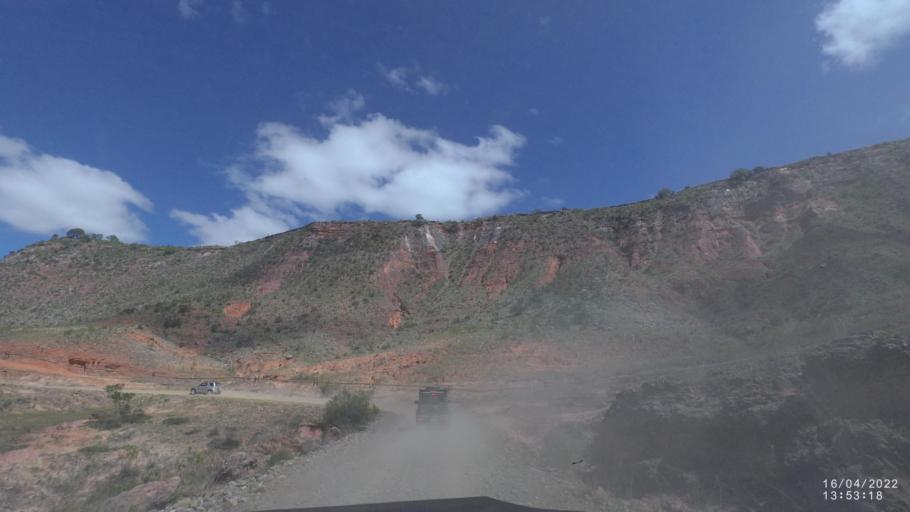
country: BO
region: Cochabamba
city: Mizque
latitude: -18.0238
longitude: -65.5715
